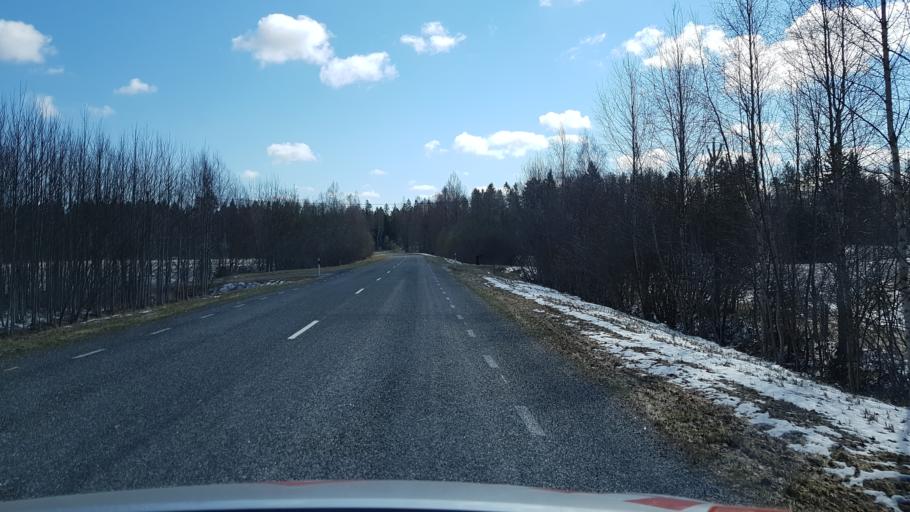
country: EE
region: Harju
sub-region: Loksa linn
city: Loksa
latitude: 59.5633
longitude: 25.9569
